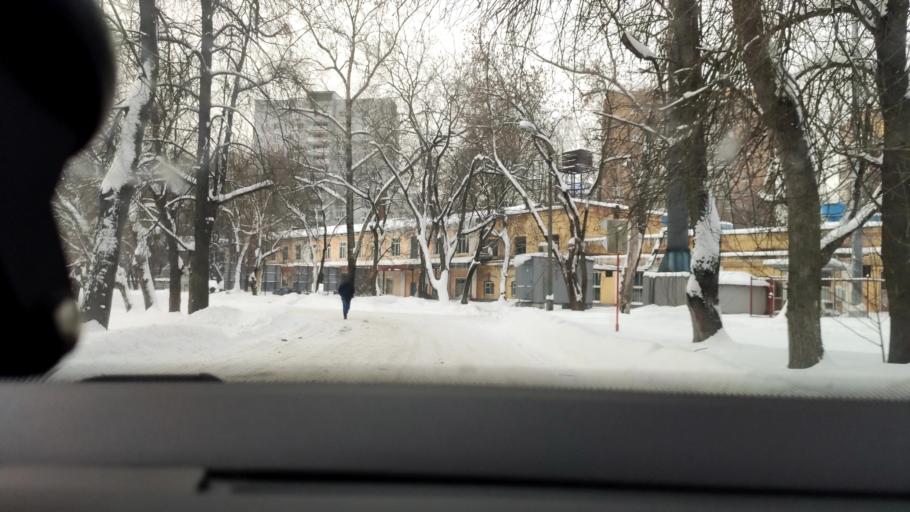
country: RU
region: Moscow
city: Yaroslavskiy
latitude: 55.8588
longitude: 37.7026
